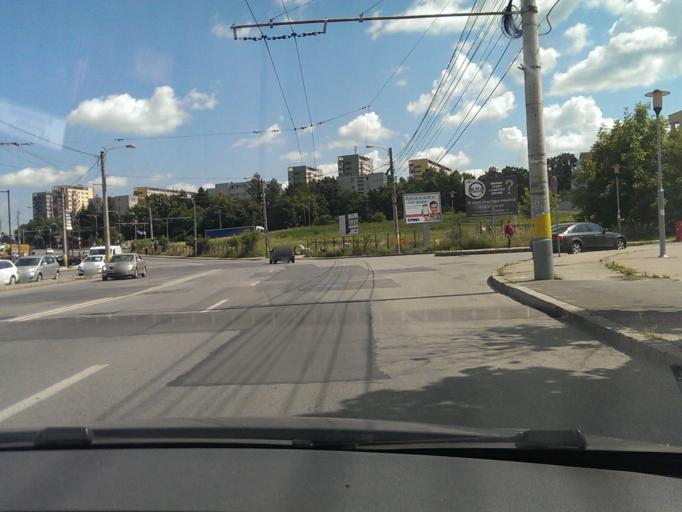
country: RO
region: Cluj
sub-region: Municipiul Cluj-Napoca
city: Cluj-Napoca
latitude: 46.7734
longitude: 23.6220
